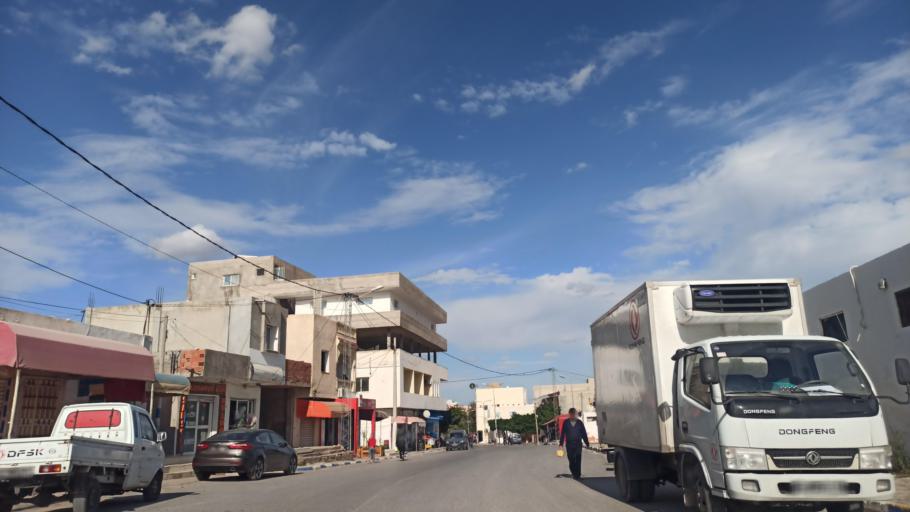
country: TN
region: Zaghwan
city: Zaghouan
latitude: 36.3508
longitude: 10.2072
